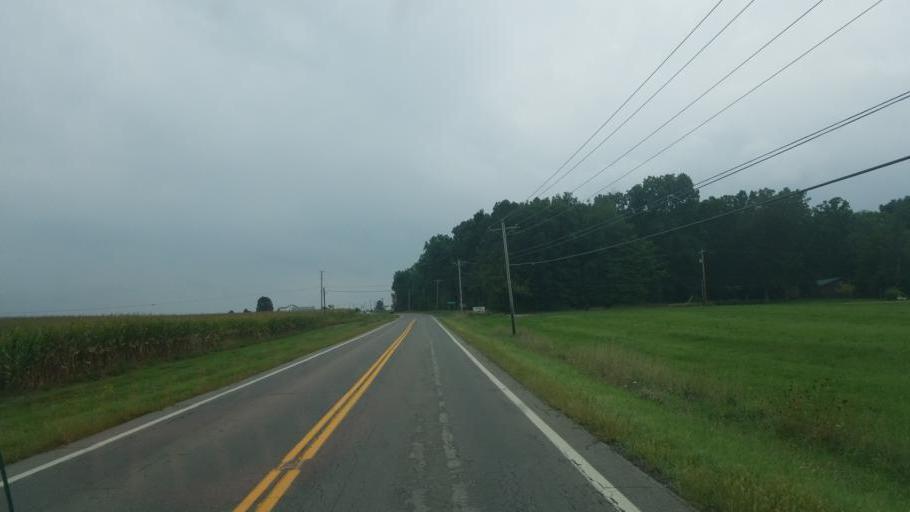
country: US
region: Ohio
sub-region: Medina County
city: Lodi
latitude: 40.9613
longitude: -81.9956
